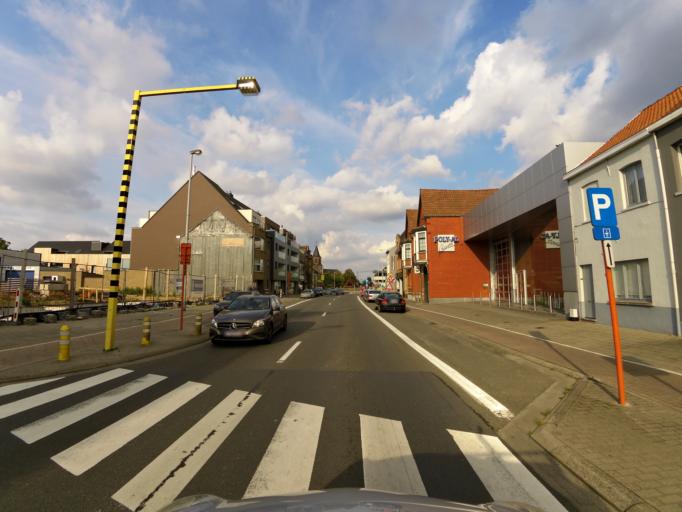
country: BE
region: Flanders
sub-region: Provincie Oost-Vlaanderen
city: Deinze
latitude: 50.9757
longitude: 3.5252
